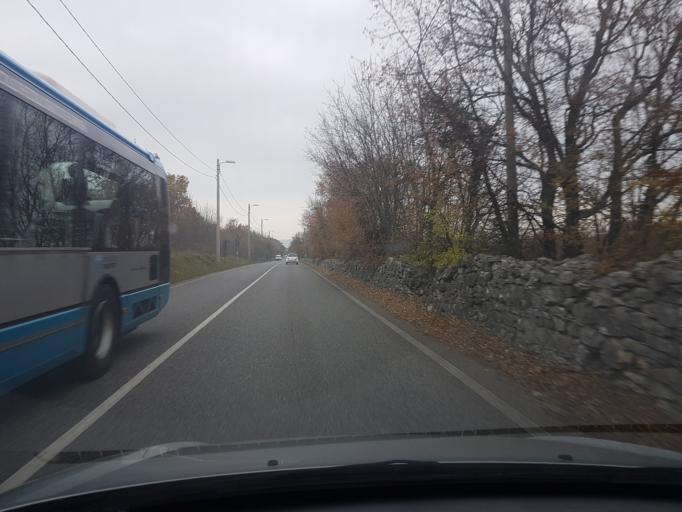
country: IT
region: Friuli Venezia Giulia
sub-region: Provincia di Trieste
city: Santa Croce
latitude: 45.7400
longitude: 13.6863
